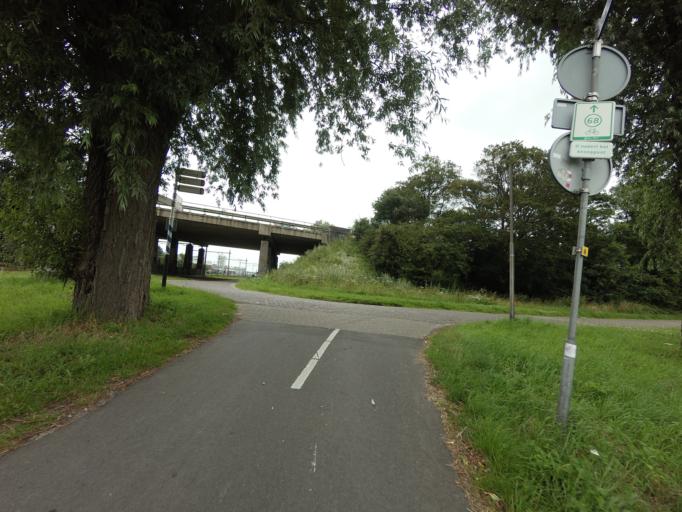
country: NL
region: South Holland
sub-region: Gemeente Teylingen
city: Voorhout
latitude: 52.2059
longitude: 4.4912
